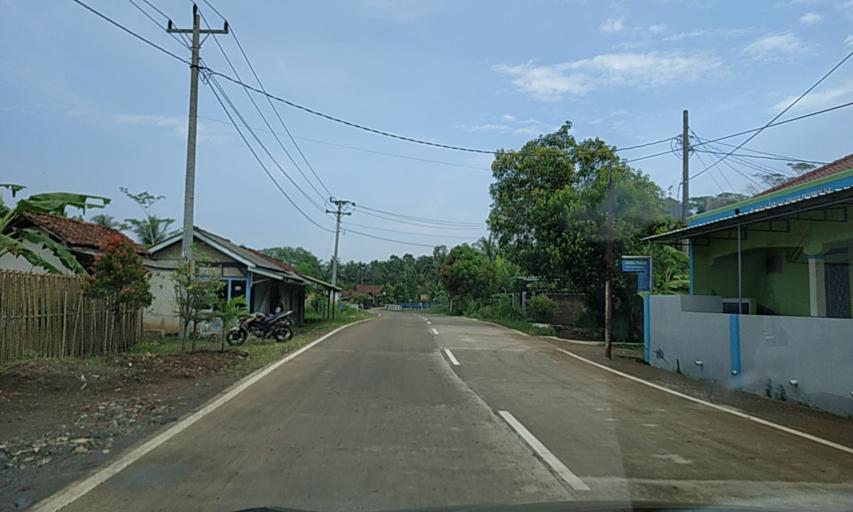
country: ID
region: Central Java
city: Ciloning
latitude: -7.4808
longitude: 108.8392
